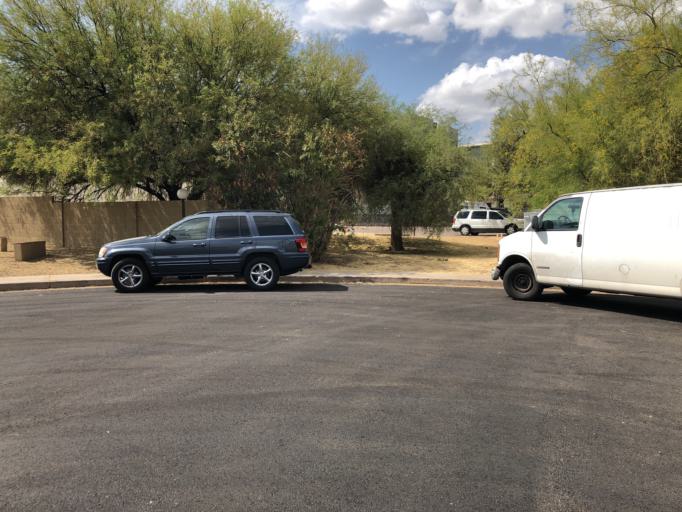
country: US
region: Arizona
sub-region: Maricopa County
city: Scottsdale
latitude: 33.4628
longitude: -111.8995
